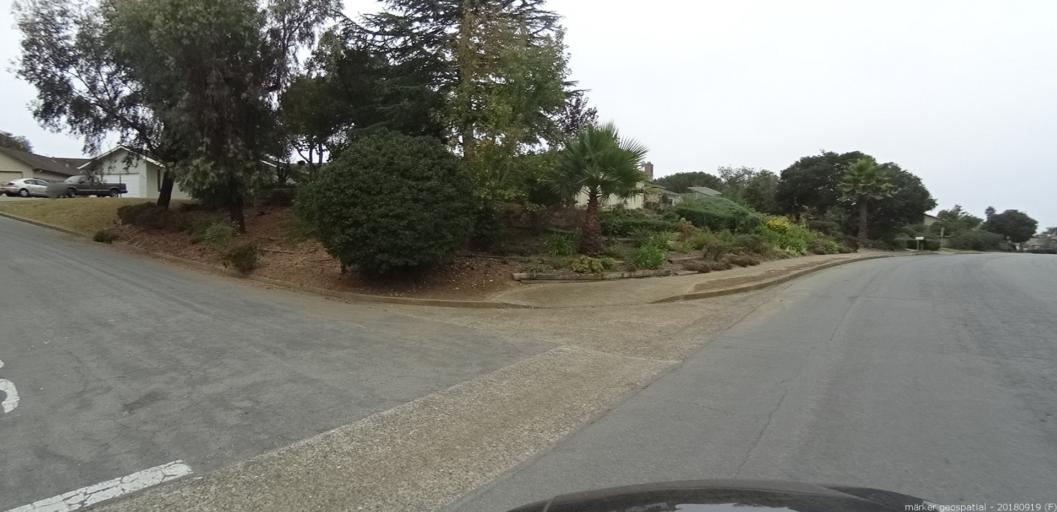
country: US
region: California
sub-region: Monterey County
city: Castroville
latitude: 36.7776
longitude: -121.7176
